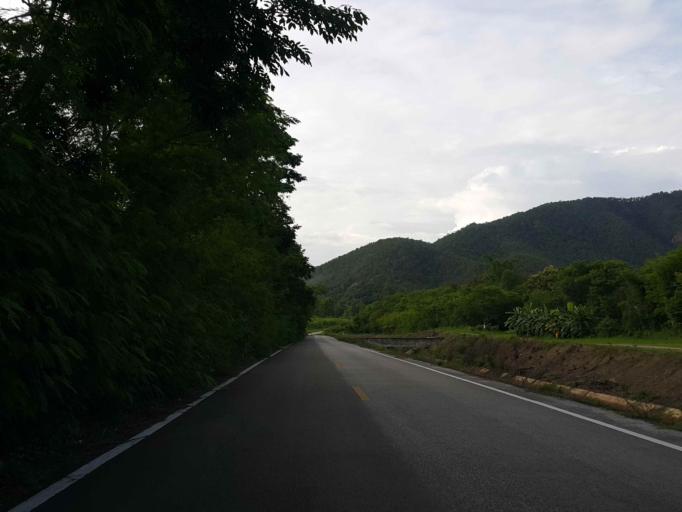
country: TH
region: Chiang Mai
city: San Sai
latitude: 18.9305
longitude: 99.1426
